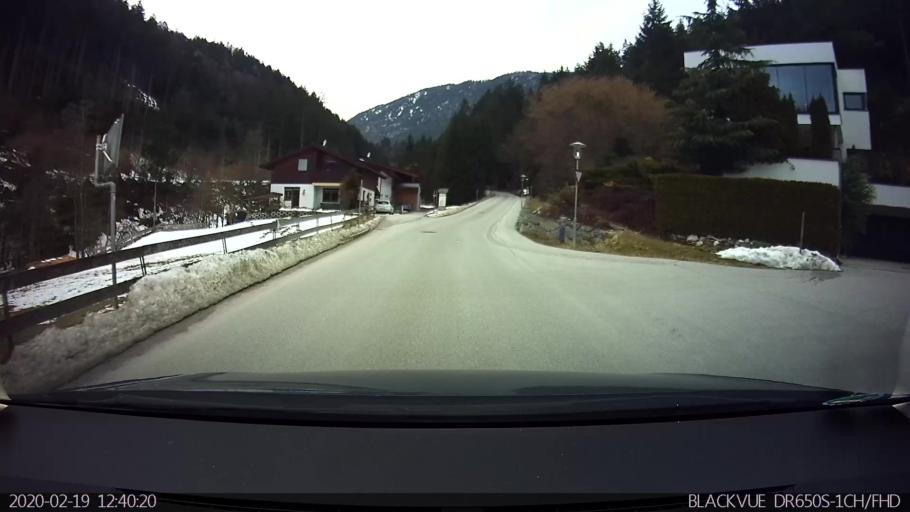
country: AT
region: Tyrol
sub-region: Politischer Bezirk Schwaz
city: Terfens
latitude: 47.3249
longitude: 11.6374
